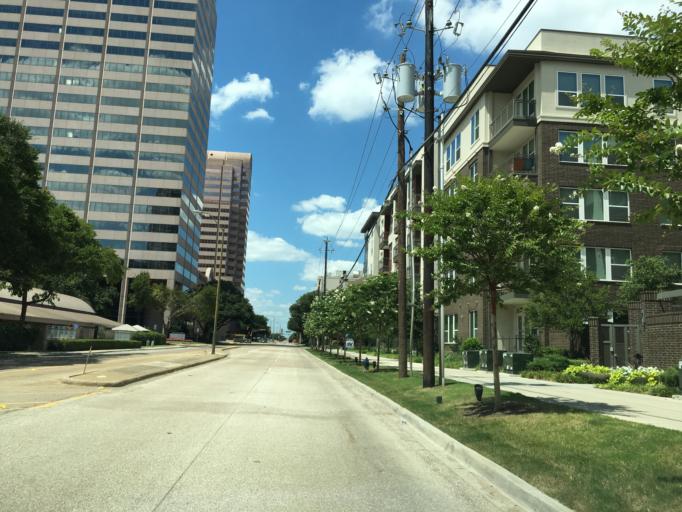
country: US
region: Texas
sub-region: Dallas County
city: Addison
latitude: 32.9281
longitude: -96.8180
